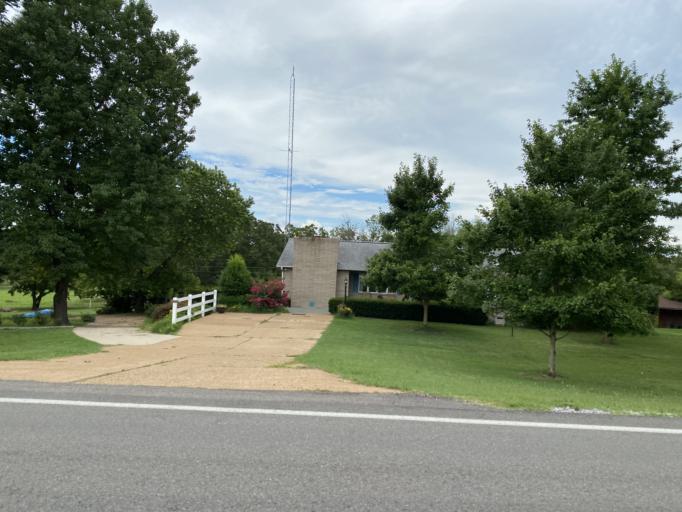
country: US
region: Arkansas
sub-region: Fulton County
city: Salem
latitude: 36.3631
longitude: -91.8301
